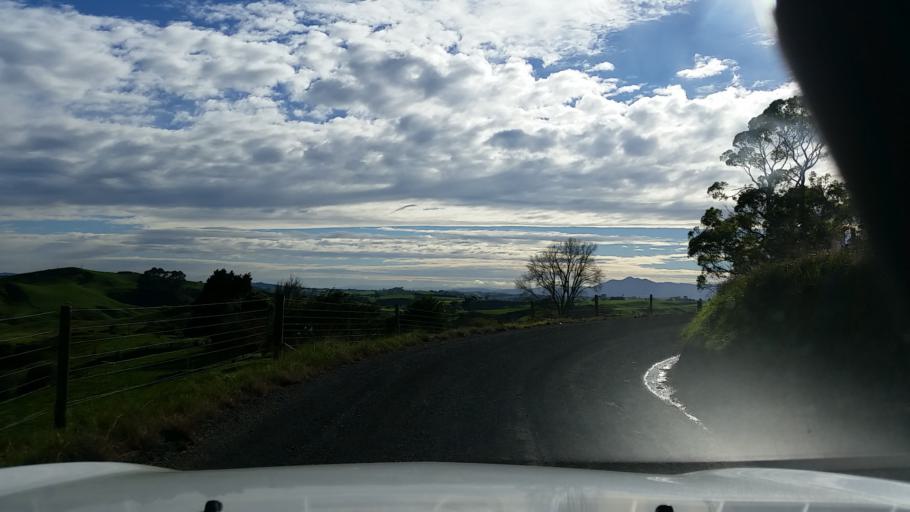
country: NZ
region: Waikato
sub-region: Matamata-Piako District
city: Matamata
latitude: -37.8199
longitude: 175.6494
